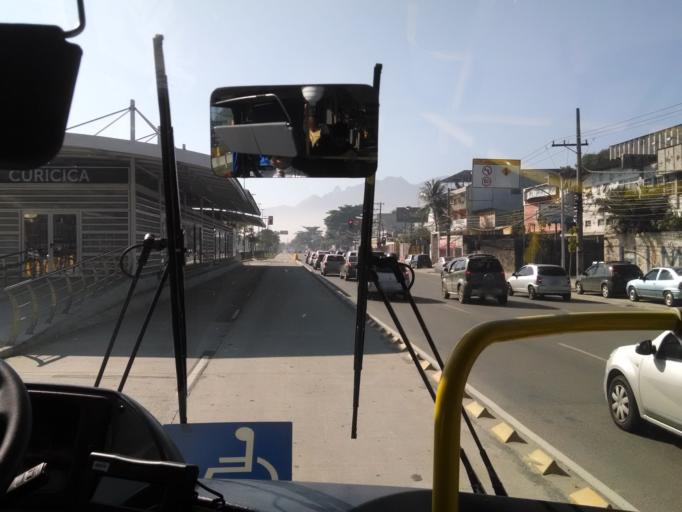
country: BR
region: Rio de Janeiro
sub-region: Nilopolis
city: Nilopolis
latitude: -22.9601
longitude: -43.3891
